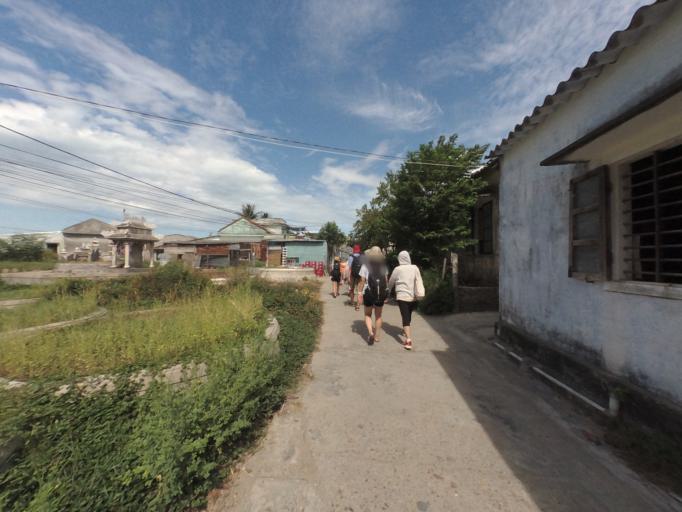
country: VN
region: Thua Thien-Hue
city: Hue
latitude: 16.5377
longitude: 107.6372
